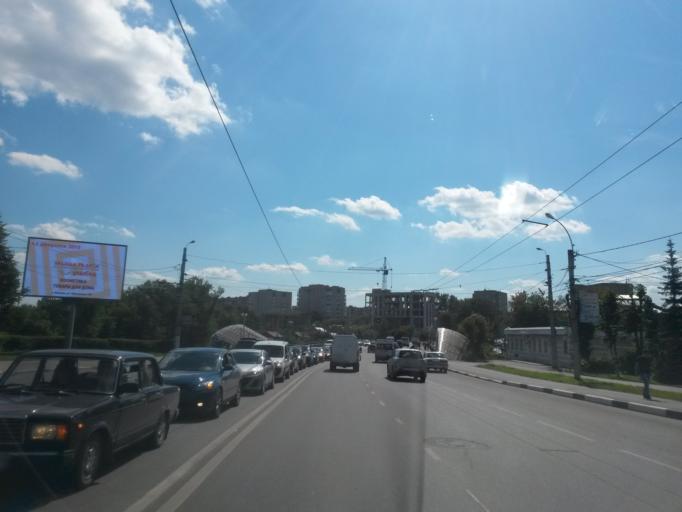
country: RU
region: Ivanovo
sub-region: Gorod Ivanovo
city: Ivanovo
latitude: 57.0059
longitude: 40.9910
